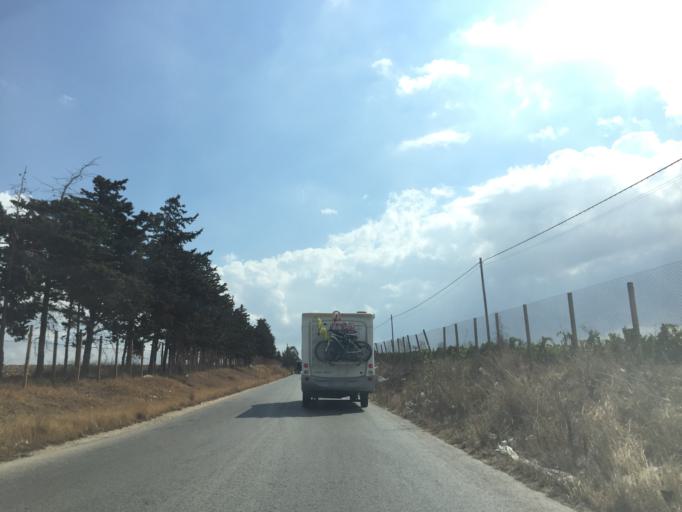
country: IT
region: Sicily
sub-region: Ragusa
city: Scoglitti
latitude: 36.9853
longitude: 14.3855
